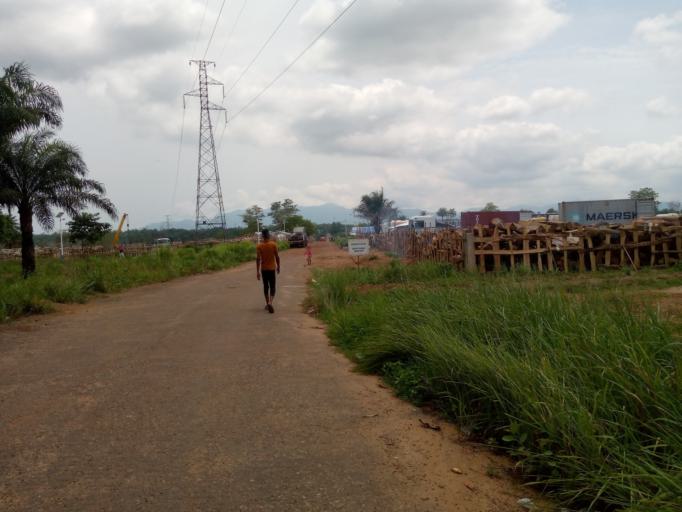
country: SL
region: Western Area
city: Waterloo
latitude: 8.3410
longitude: -12.9862
